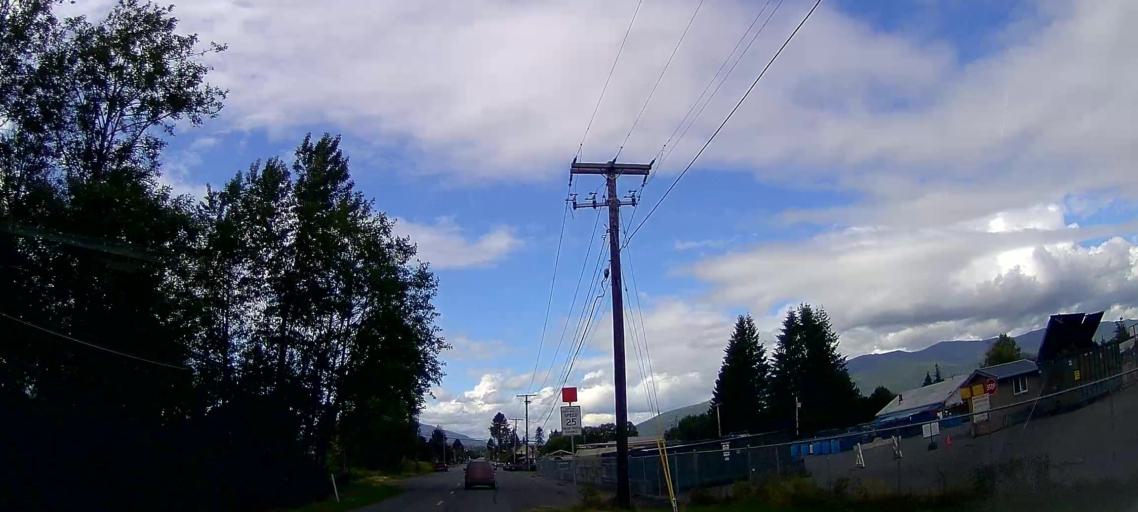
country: US
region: Washington
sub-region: Skagit County
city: Sedro-Woolley
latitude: 48.4963
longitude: -122.2375
